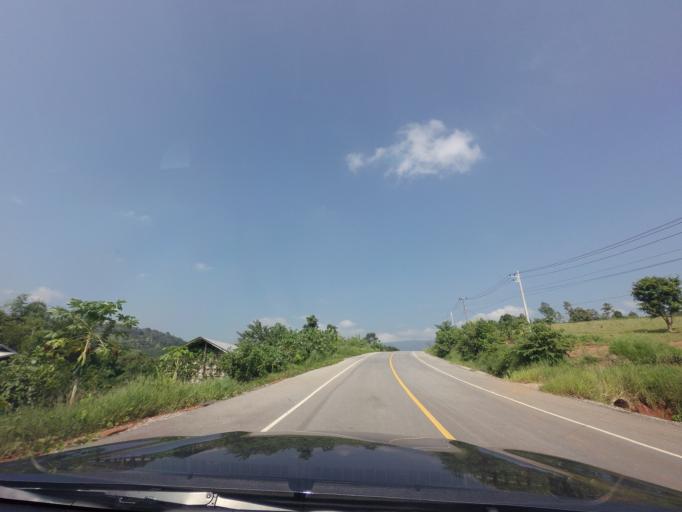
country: TH
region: Loei
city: Na Haeo
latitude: 17.4952
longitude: 101.0272
